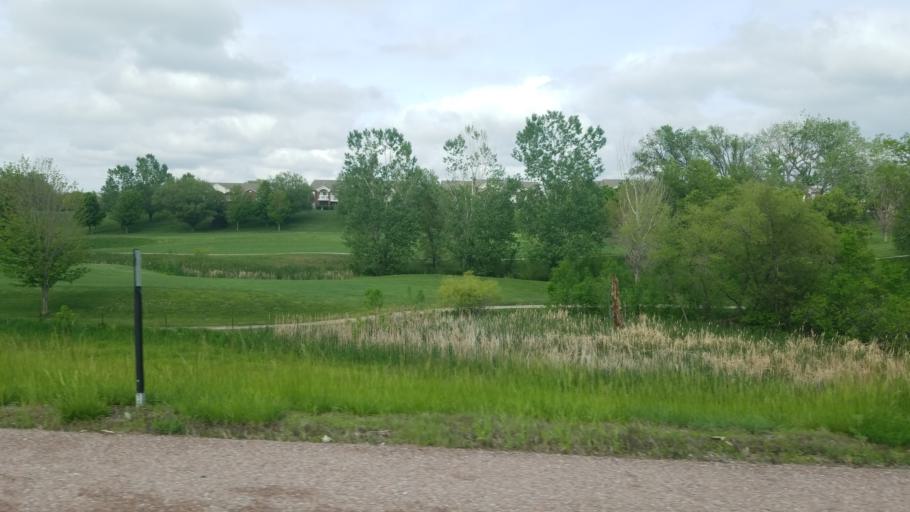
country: US
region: Nebraska
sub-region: Lancaster County
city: Lincoln
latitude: 40.8662
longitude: -96.7177
